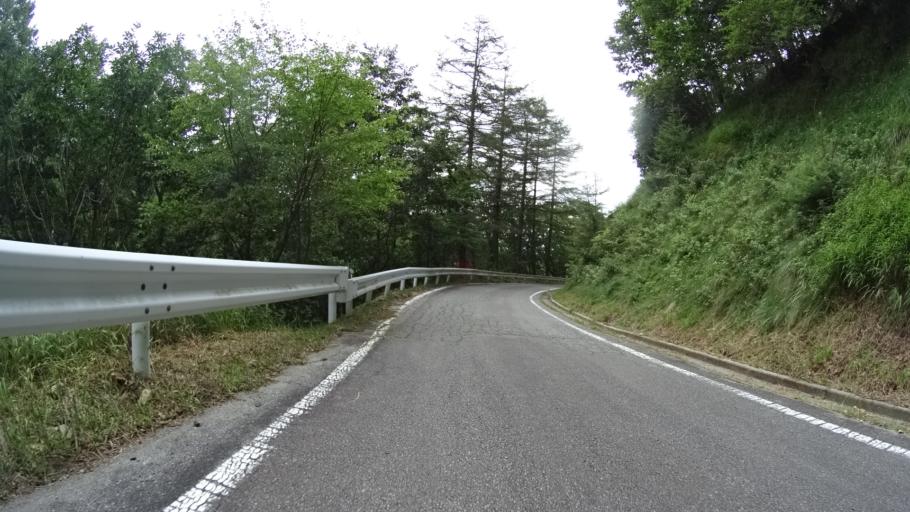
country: JP
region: Yamanashi
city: Kofu-shi
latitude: 35.8303
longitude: 138.5645
